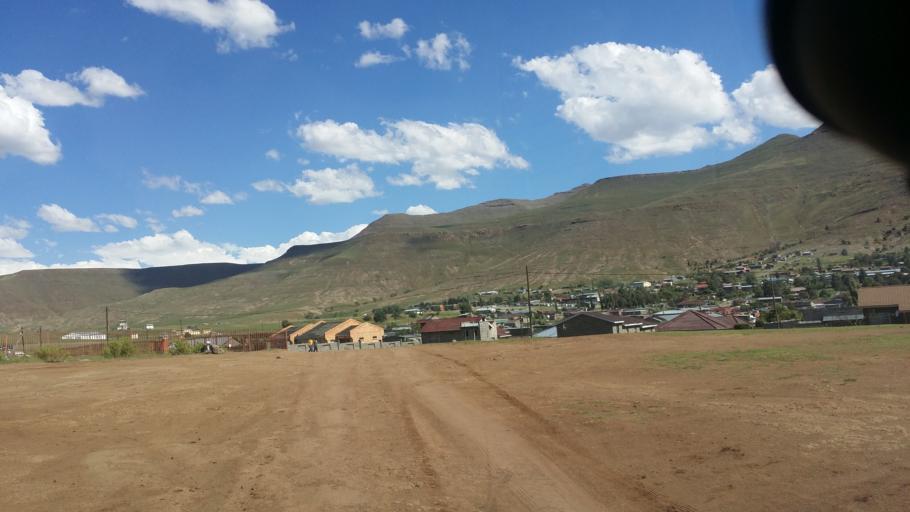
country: LS
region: Mokhotlong
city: Mokhotlong
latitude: -29.2797
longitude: 29.0658
